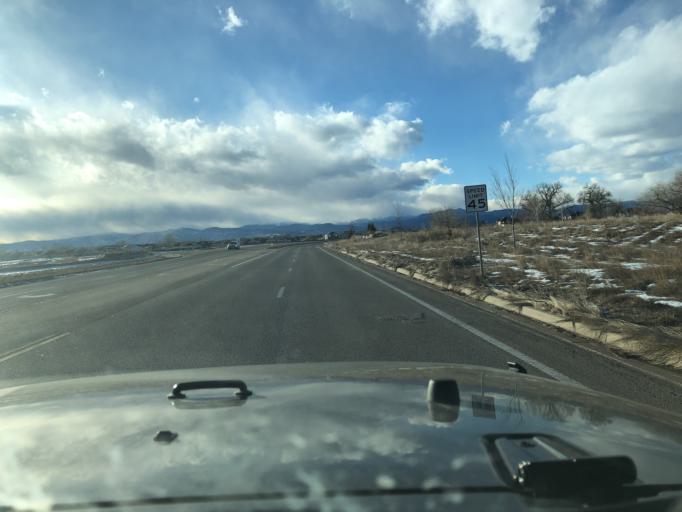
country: US
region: Colorado
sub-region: Boulder County
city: Longmont
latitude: 40.1878
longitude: -105.0562
